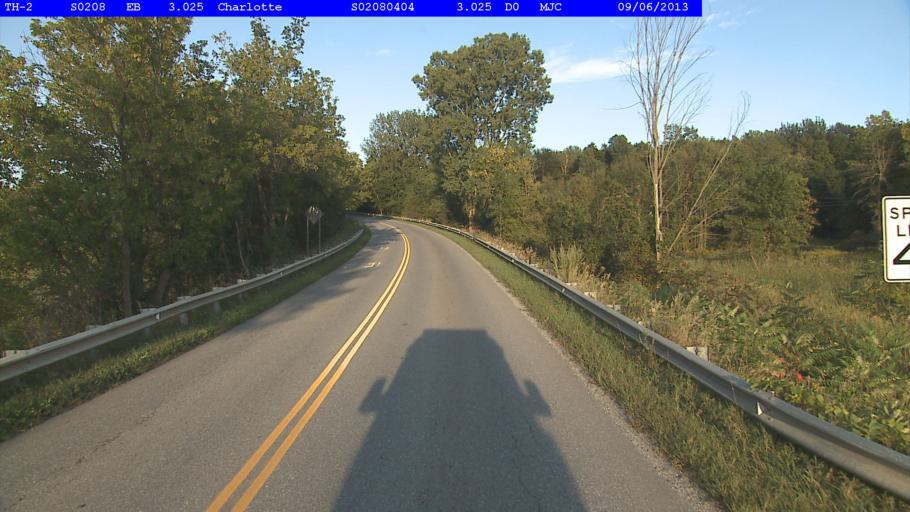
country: US
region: Vermont
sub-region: Chittenden County
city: Hinesburg
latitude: 44.3197
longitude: -73.1880
